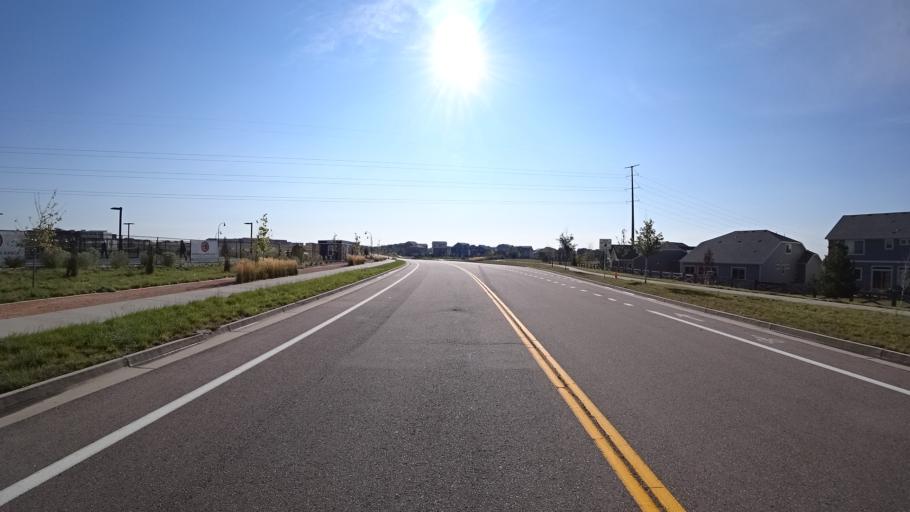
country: US
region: Colorado
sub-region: El Paso County
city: Cimarron Hills
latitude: 38.9304
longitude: -104.6646
